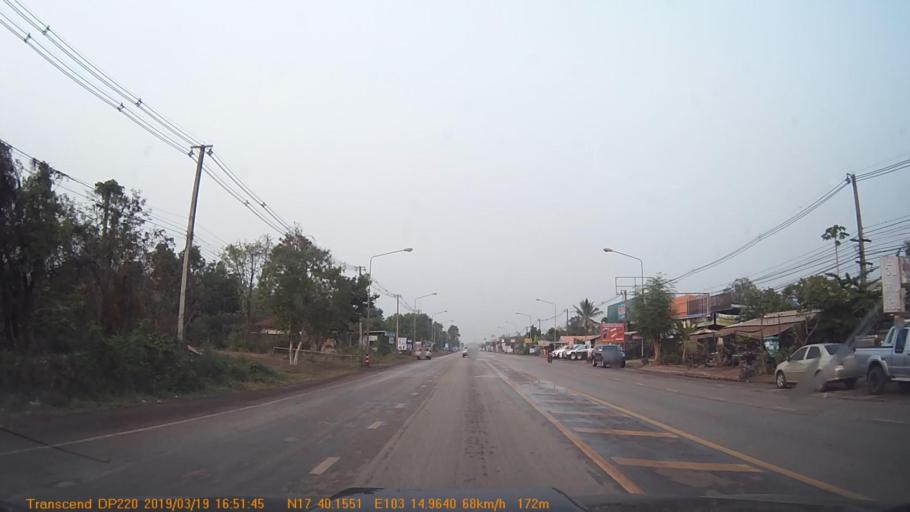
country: TH
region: Changwat Udon Thani
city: Ban Dung
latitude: 17.6697
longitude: 103.2496
